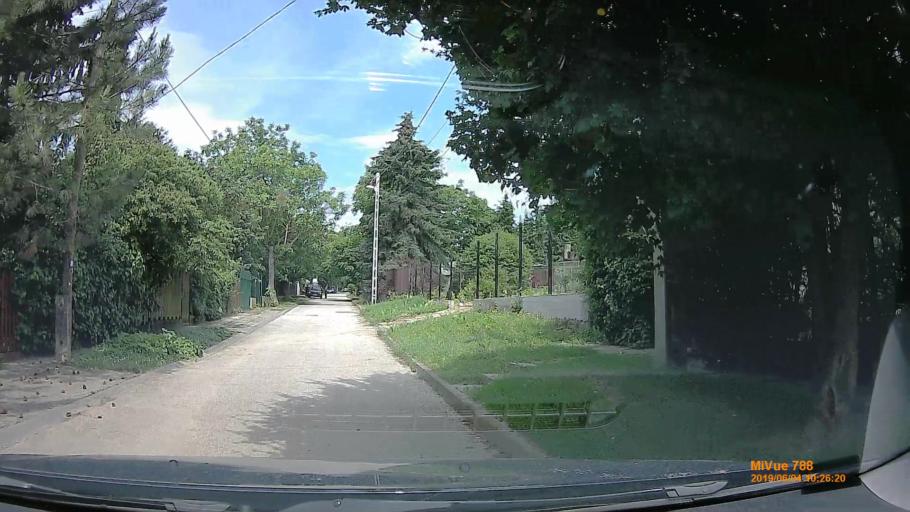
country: HU
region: Budapest
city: Budapest XXII. keruelet
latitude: 47.4437
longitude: 19.0175
